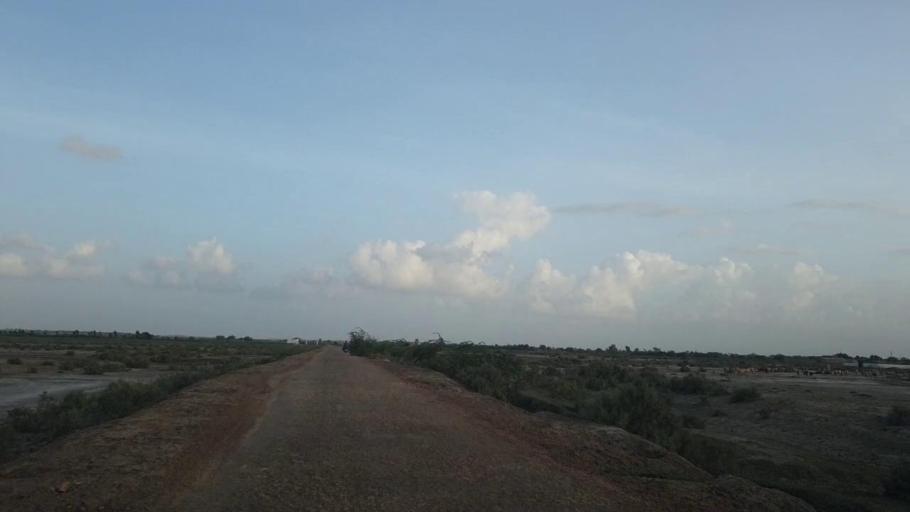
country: PK
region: Sindh
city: Kadhan
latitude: 24.5539
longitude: 69.1233
